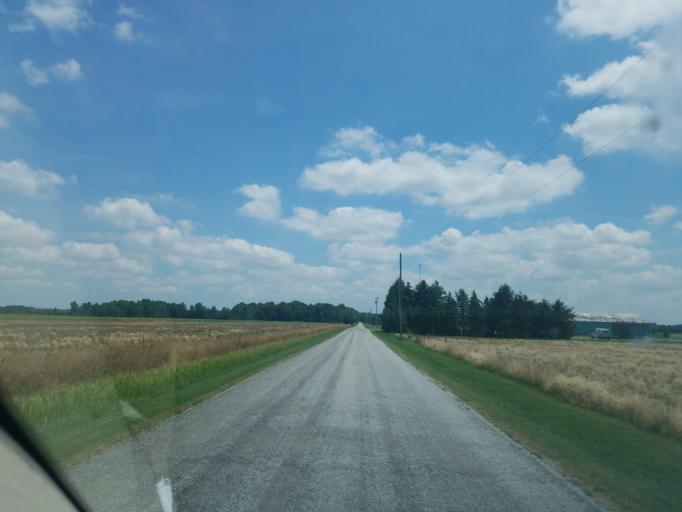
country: US
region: Ohio
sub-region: Hardin County
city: Forest
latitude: 40.7753
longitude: -83.6231
